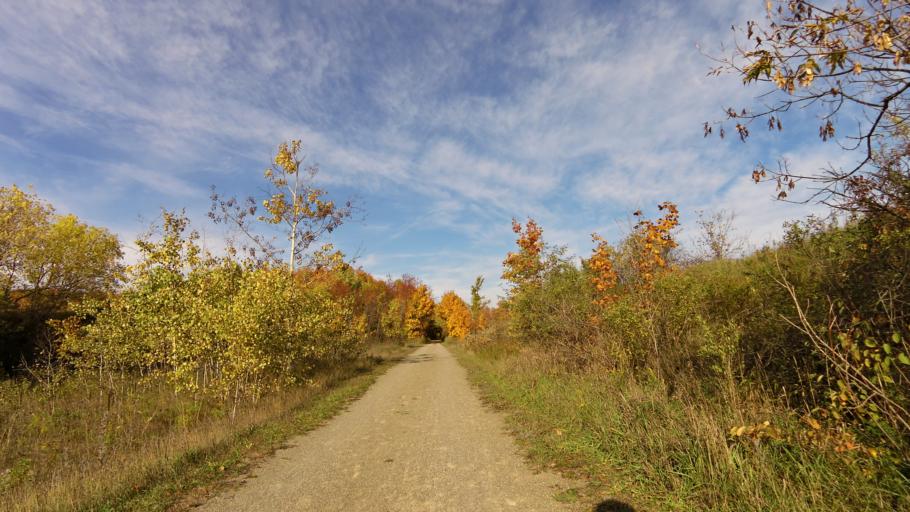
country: CA
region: Ontario
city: Orangeville
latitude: 43.8033
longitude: -80.0348
